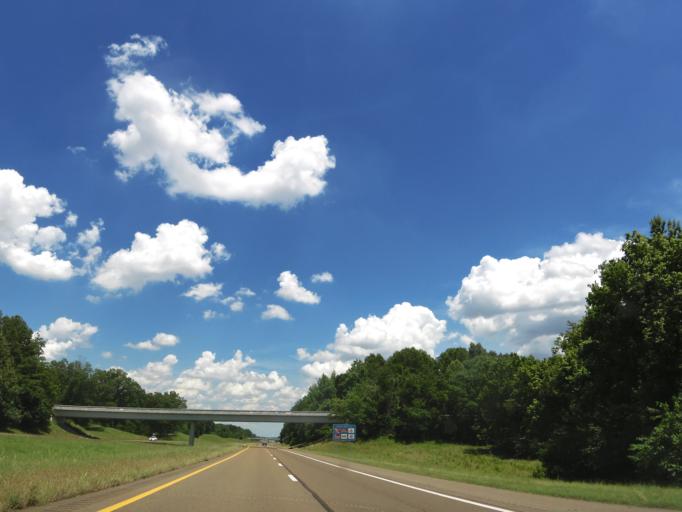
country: US
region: Tennessee
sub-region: Dyer County
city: Dyersburg
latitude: 36.0694
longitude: -89.4281
